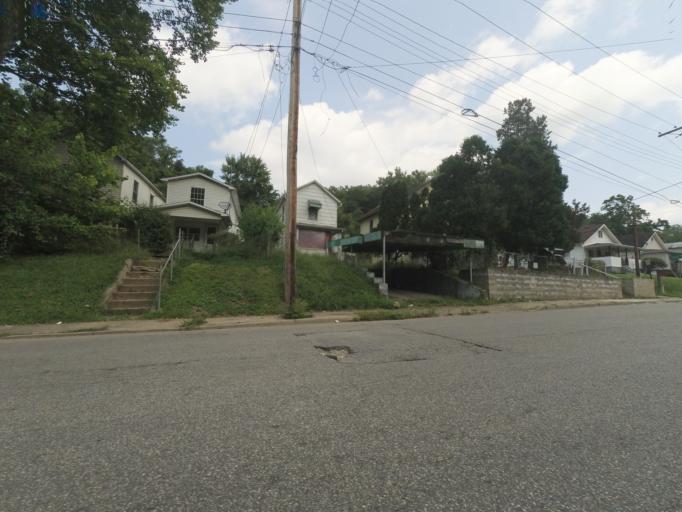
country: US
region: West Virginia
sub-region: Cabell County
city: Huntington
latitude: 38.4178
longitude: -82.4074
